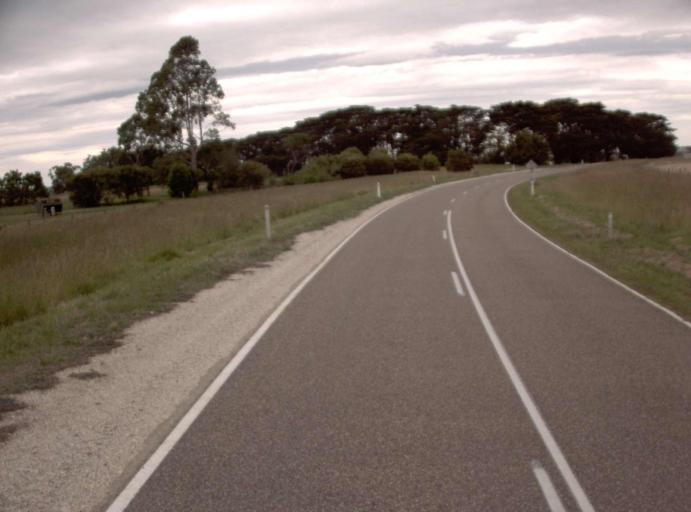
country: AU
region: Victoria
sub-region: Wellington
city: Sale
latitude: -38.0486
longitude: 147.1513
